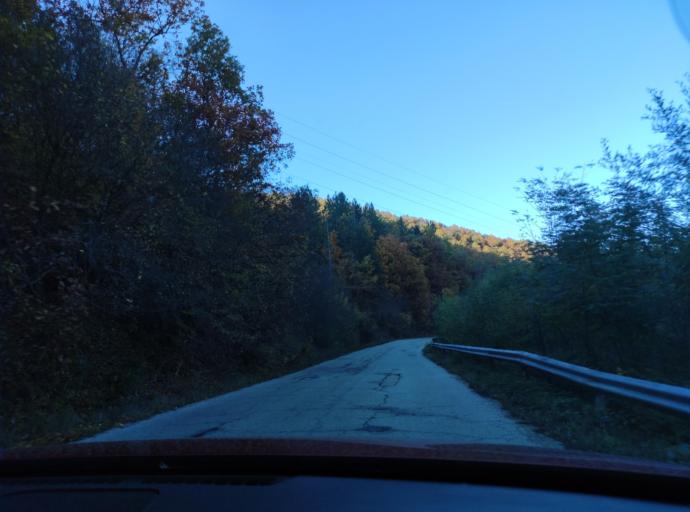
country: BG
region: Montana
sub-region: Obshtina Chiprovtsi
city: Chiprovtsi
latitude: 43.4100
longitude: 22.9389
